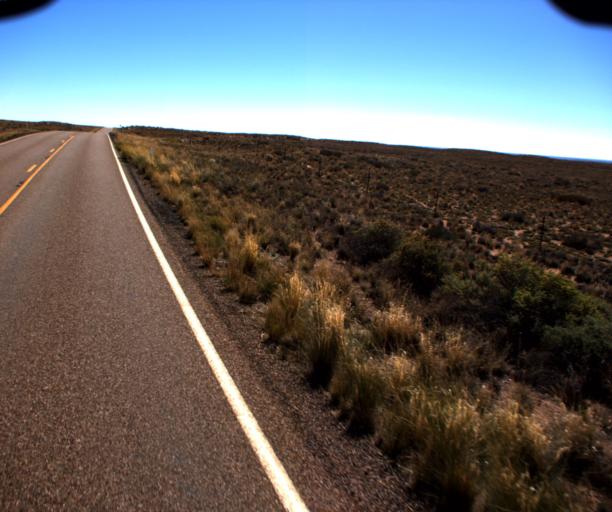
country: US
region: Arizona
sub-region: Navajo County
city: Holbrook
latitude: 35.0362
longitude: -110.0910
